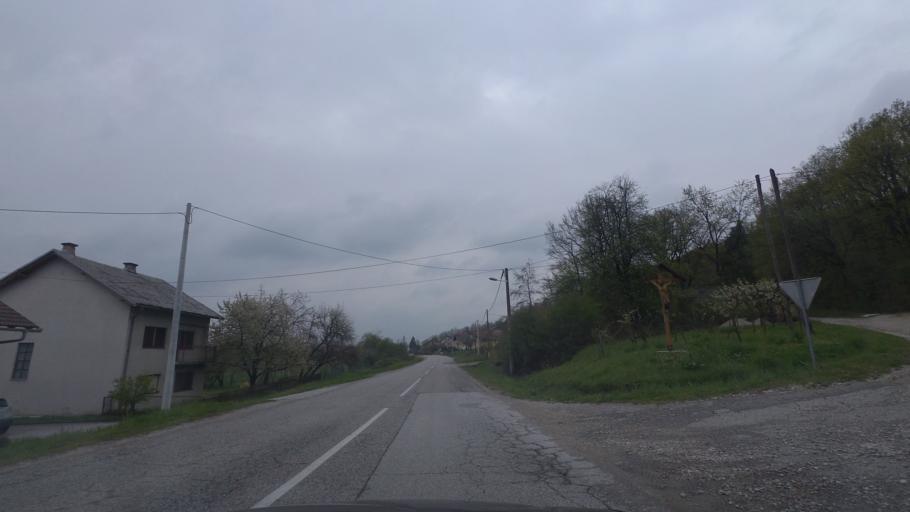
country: HR
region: Karlovacka
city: Ozalj
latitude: 45.6385
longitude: 15.5351
